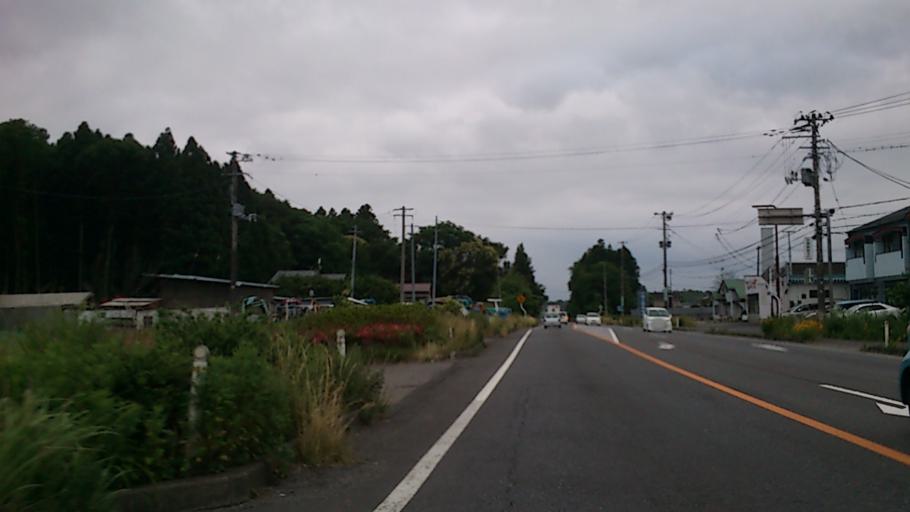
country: JP
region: Fukushima
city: Sukagawa
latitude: 37.2477
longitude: 140.3378
